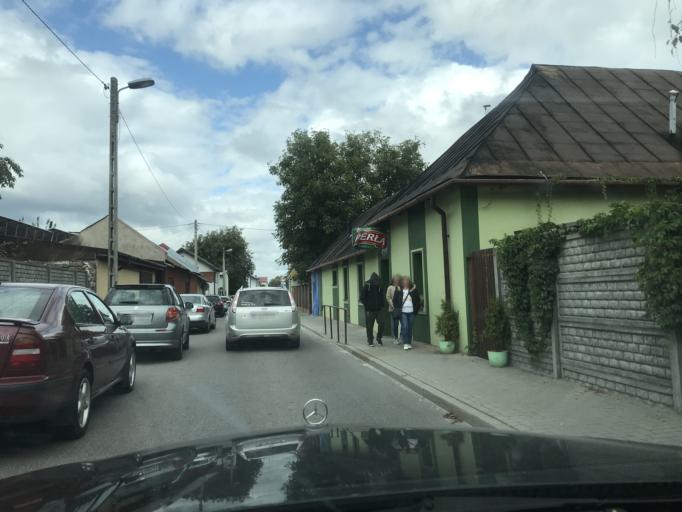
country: PL
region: Lublin Voivodeship
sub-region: Powiat janowski
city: Janow Lubelski
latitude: 50.7059
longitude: 22.4146
